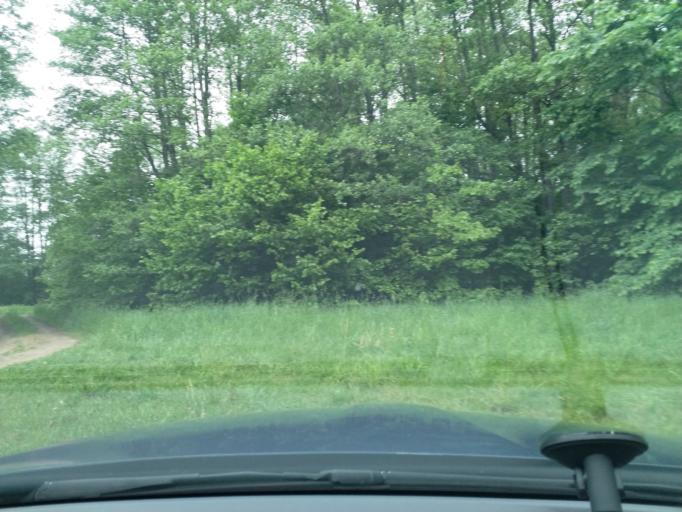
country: LV
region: Kuldigas Rajons
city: Kuldiga
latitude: 56.8749
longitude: 21.8228
